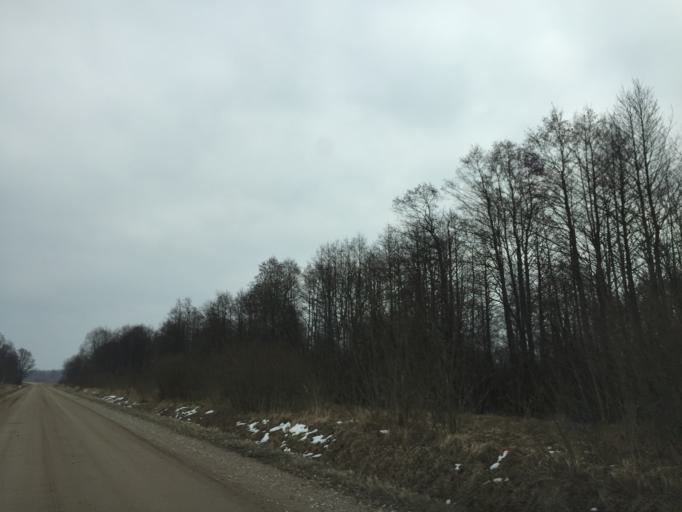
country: LV
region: Salacgrivas
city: Ainazi
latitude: 58.0314
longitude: 24.4655
